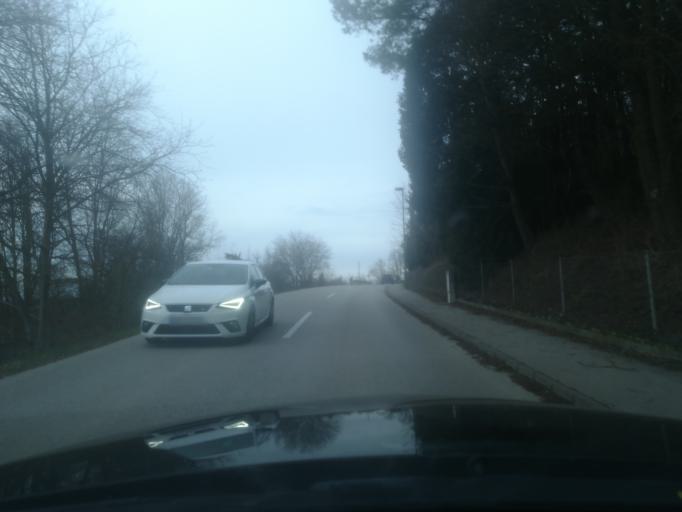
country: AT
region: Upper Austria
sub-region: Wels-Land
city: Steinhaus
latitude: 48.1346
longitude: 14.0092
